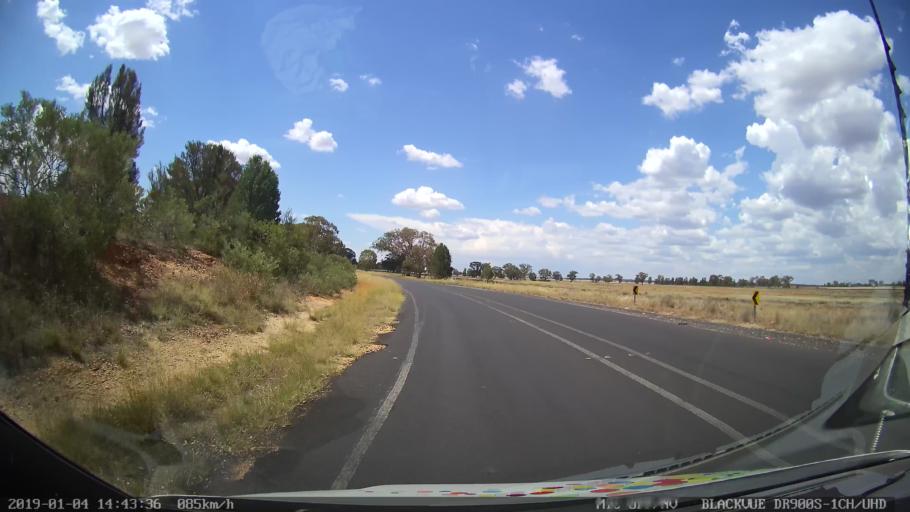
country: AU
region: New South Wales
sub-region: Dubbo Municipality
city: Dubbo
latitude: -32.1169
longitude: 148.6536
